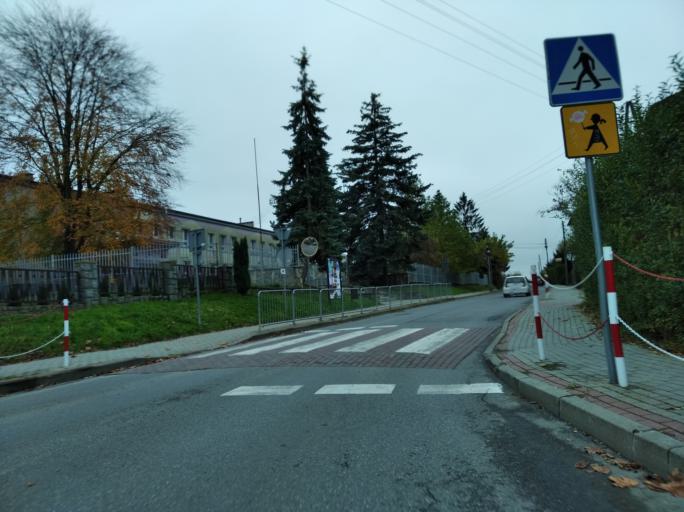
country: PL
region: Subcarpathian Voivodeship
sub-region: Krosno
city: Krosno
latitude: 49.6934
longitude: 21.7582
